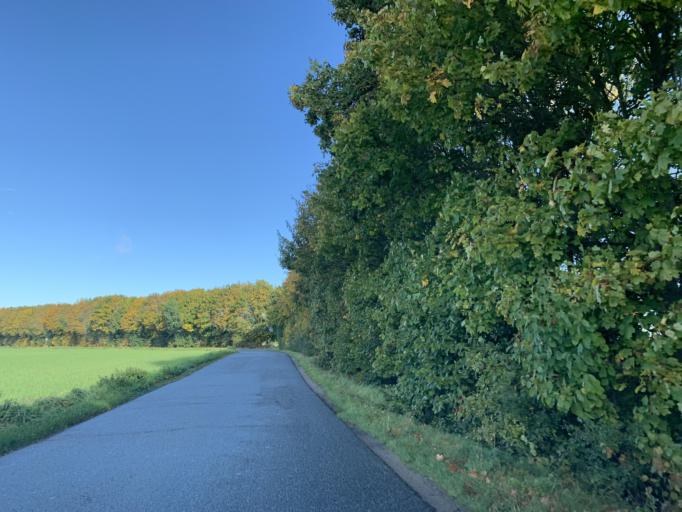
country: DE
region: Mecklenburg-Vorpommern
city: Gross Nemerow
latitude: 53.4716
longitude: 13.2693
